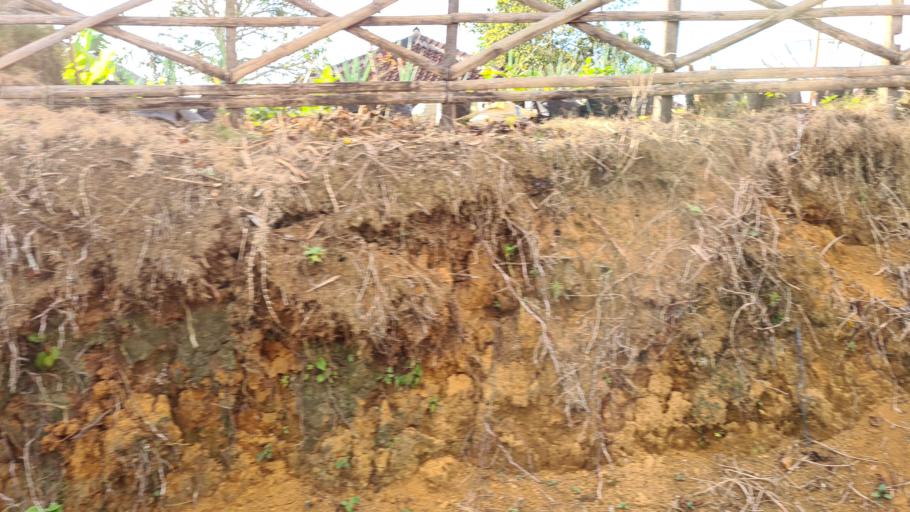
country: ID
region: Lampung
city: Kenali
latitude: -5.0958
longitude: 104.3976
